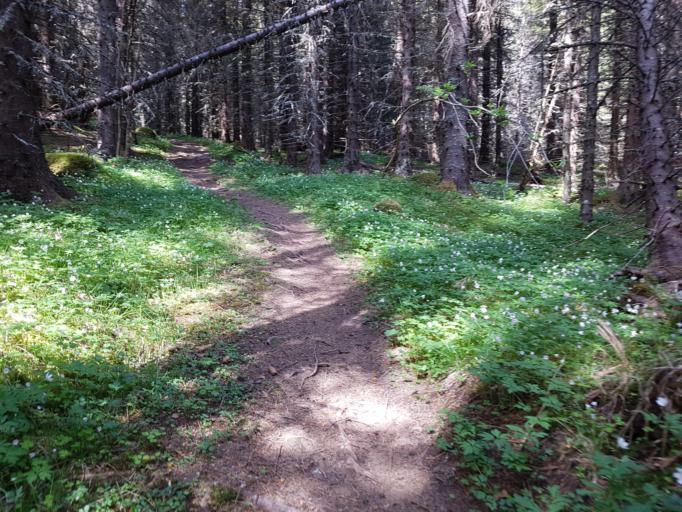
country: NO
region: Sor-Trondelag
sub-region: Trondheim
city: Trondheim
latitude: 63.4254
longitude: 10.3341
